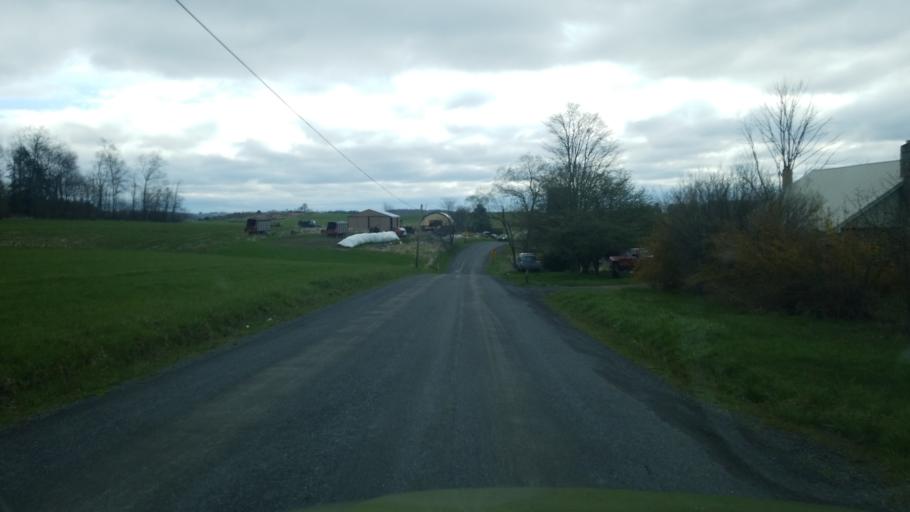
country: US
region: Pennsylvania
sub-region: Clearfield County
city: Clearfield
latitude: 41.0831
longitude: -78.4021
